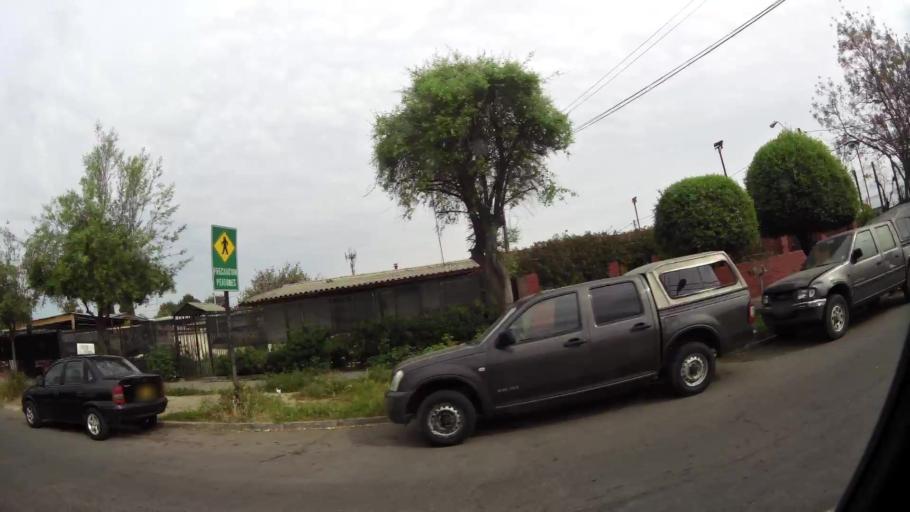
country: CL
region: Santiago Metropolitan
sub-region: Provincia de Santiago
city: Lo Prado
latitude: -33.5242
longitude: -70.7619
